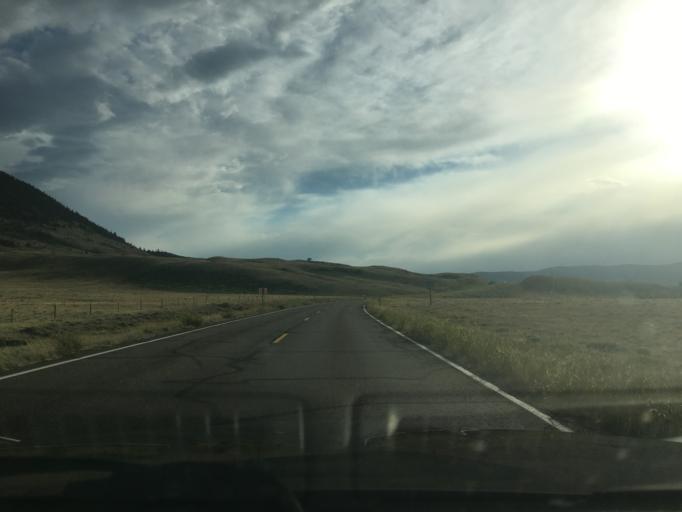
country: US
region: Wyoming
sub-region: Albany County
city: Laramie
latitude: 41.2867
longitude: -106.0410
